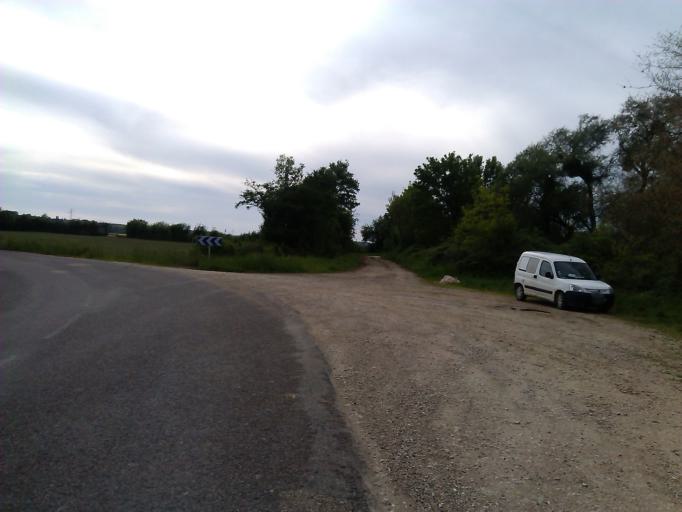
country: FR
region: Franche-Comte
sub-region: Departement du Jura
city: Dampierre
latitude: 47.1385
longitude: 5.7096
